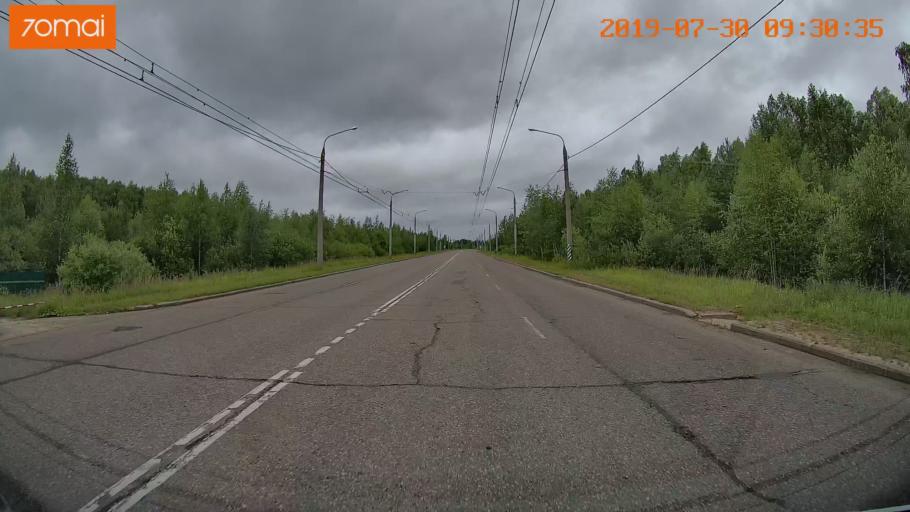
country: RU
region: Ivanovo
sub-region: Gorod Ivanovo
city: Ivanovo
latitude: 56.9462
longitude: 40.9468
